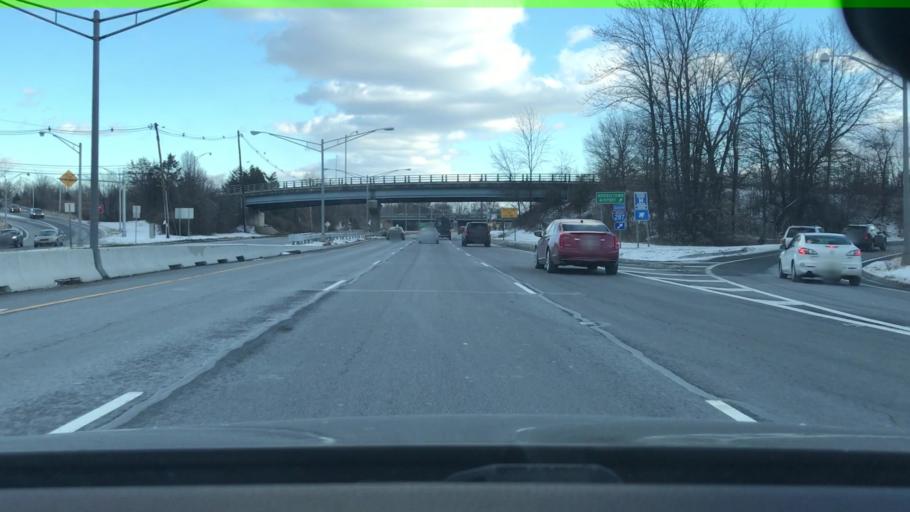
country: US
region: New Jersey
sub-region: Morris County
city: Parsippany
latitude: 40.8342
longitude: -74.4418
